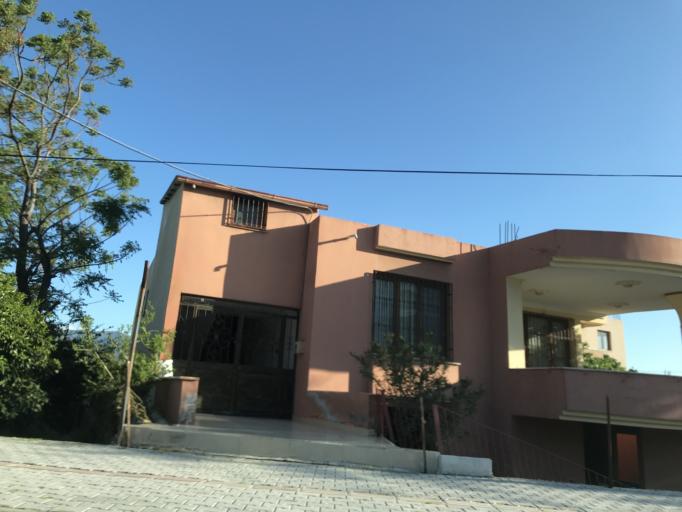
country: TR
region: Hatay
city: Samandag
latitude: 36.0832
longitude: 35.9592
